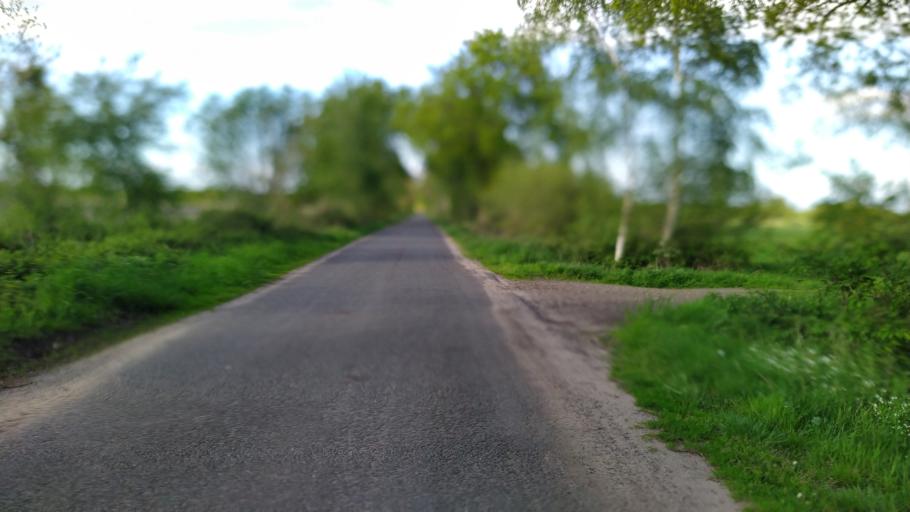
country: DE
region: Lower Saxony
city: Farven
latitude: 53.4216
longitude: 9.3359
